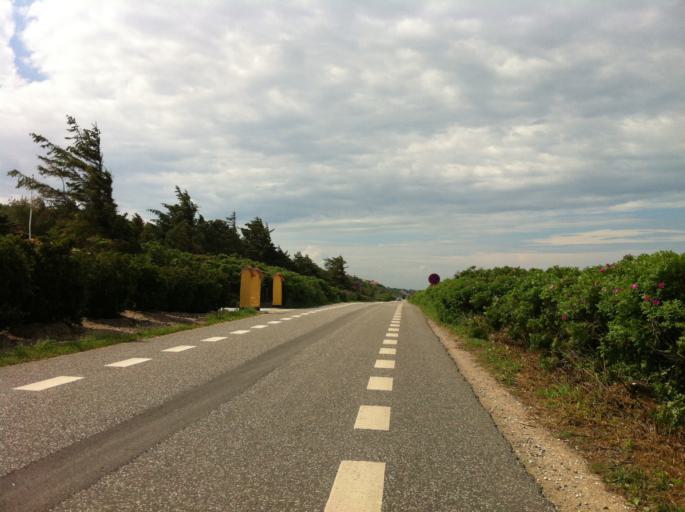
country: DK
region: Capital Region
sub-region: Gribskov Kommune
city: Helsinge
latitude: 56.1059
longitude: 12.1756
